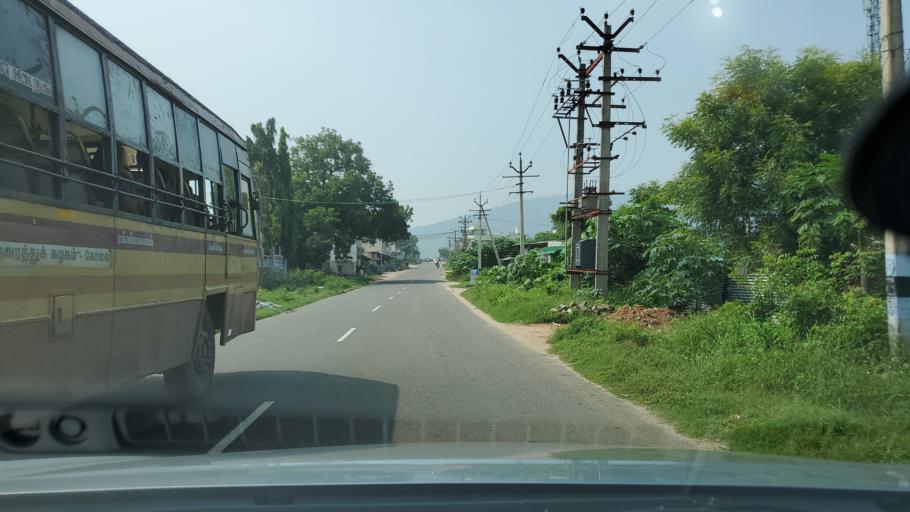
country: IN
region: Tamil Nadu
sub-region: Erode
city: Chennimalai
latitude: 11.1721
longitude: 77.6045
